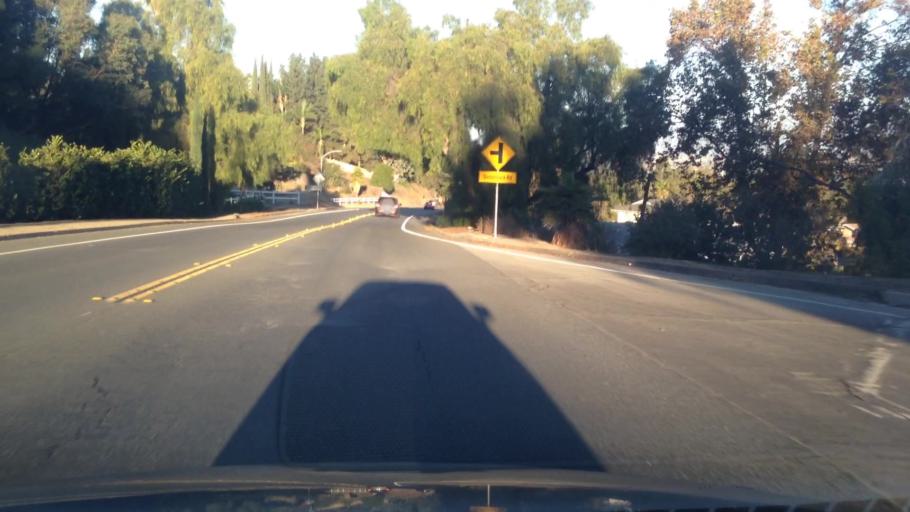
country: US
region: California
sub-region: Riverside County
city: Woodcrest
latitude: 33.8928
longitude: -117.3754
